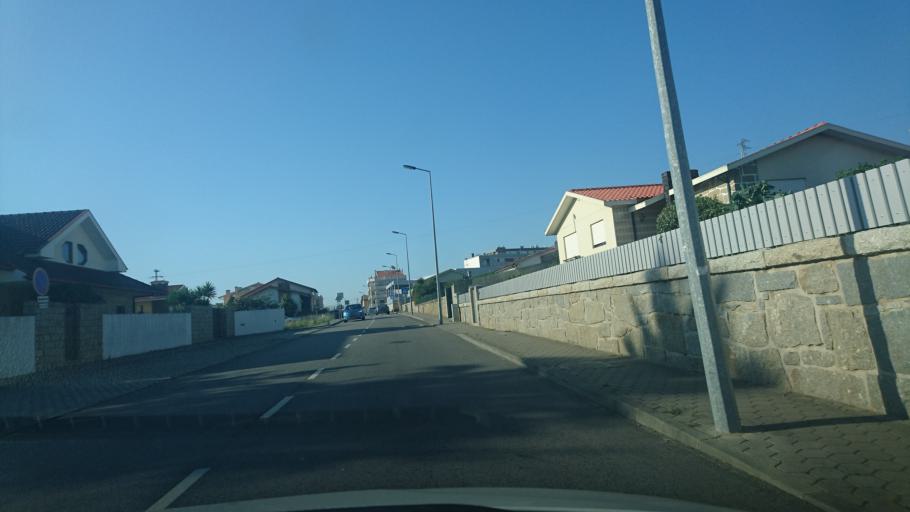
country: PT
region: Aveiro
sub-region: Ovar
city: Esmoriz
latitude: 40.9601
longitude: -8.6296
